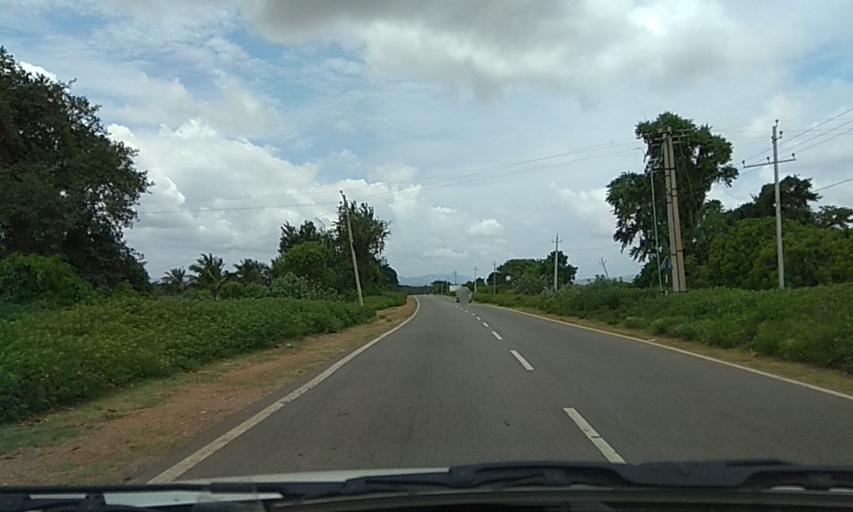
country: IN
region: Karnataka
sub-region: Chamrajnagar
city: Gundlupet
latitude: 11.8152
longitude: 76.7538
